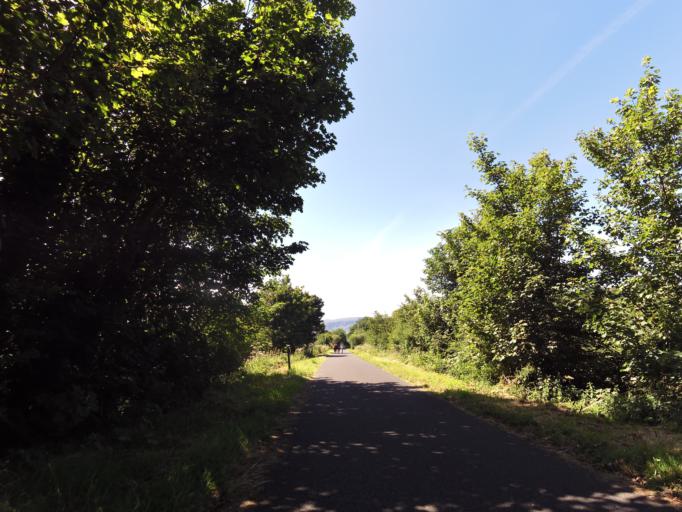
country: IE
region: Munster
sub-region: Waterford
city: Portlaw
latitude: 52.2039
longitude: -7.4154
